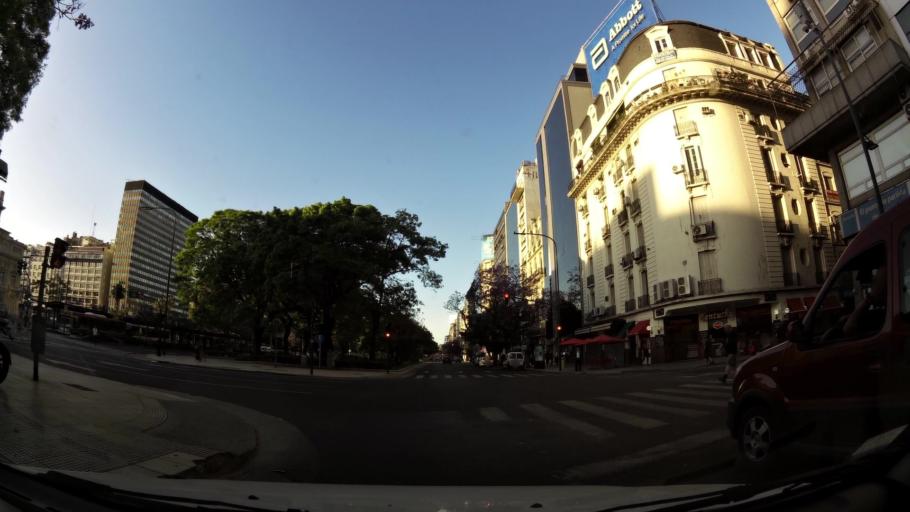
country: AR
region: Buenos Aires F.D.
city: Buenos Aires
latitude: -34.6015
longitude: -58.3812
